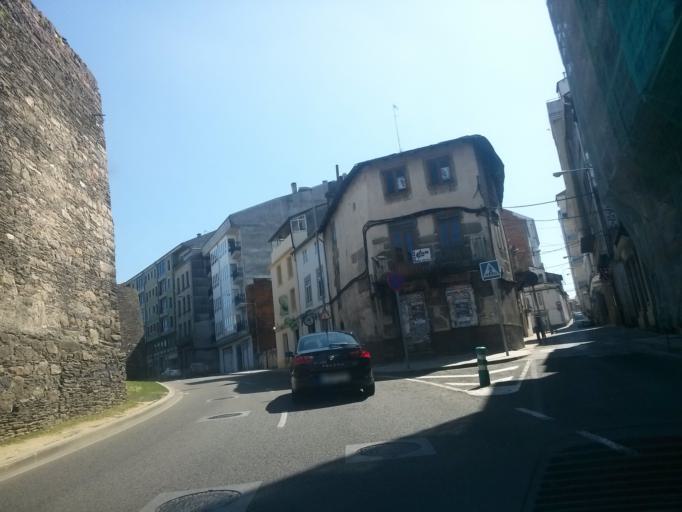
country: ES
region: Galicia
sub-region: Provincia de Lugo
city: Lugo
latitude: 43.0084
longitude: -7.5591
